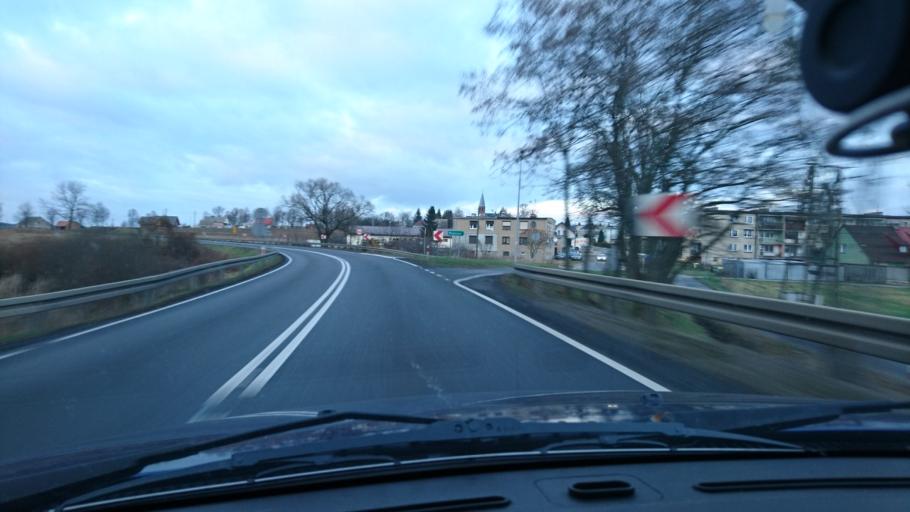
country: PL
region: Greater Poland Voivodeship
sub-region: Powiat ostrzeszowski
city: Ostrzeszow
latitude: 51.3836
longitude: 17.9494
